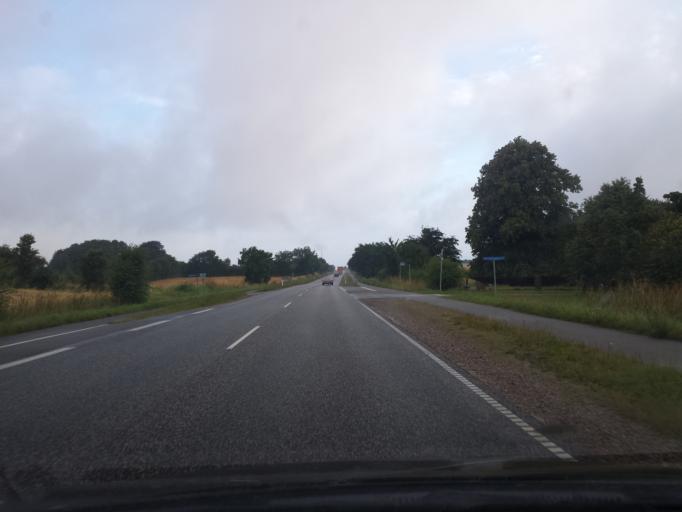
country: DK
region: South Denmark
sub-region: Sonderborg Kommune
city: Guderup
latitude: 55.0072
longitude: 9.8458
